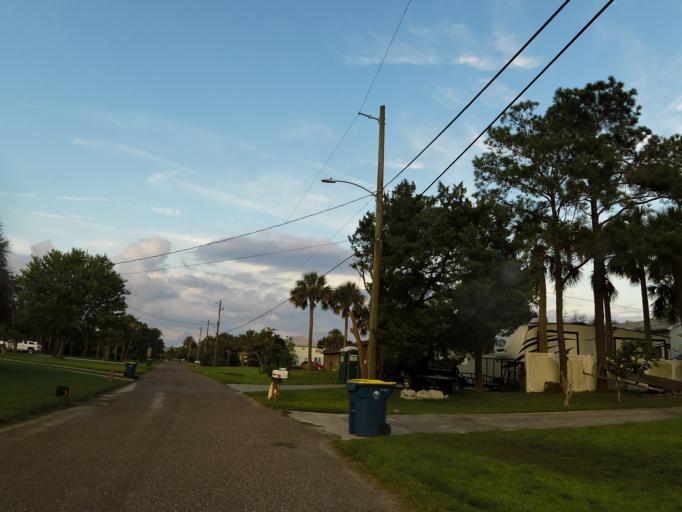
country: US
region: Florida
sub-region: Duval County
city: Atlantic Beach
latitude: 30.3938
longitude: -81.4954
